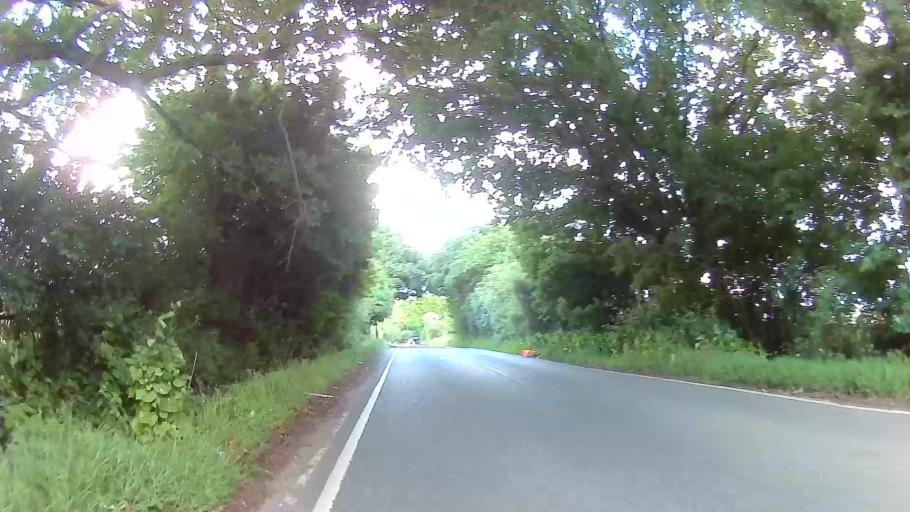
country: GB
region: England
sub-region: Greater London
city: Collier Row
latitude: 51.6319
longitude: 0.1929
